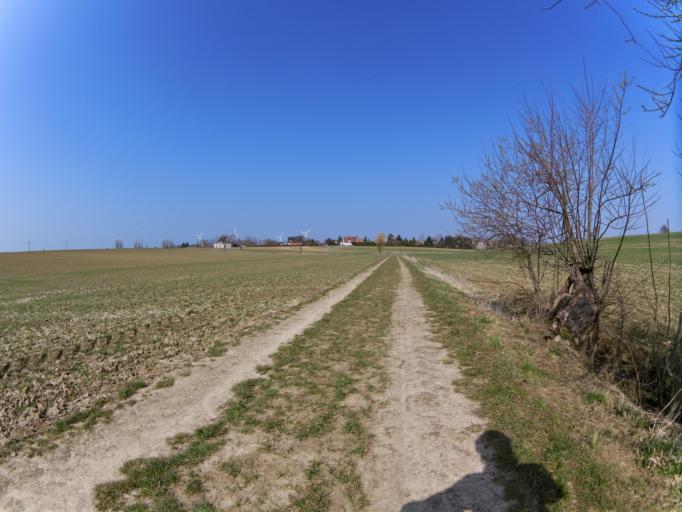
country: DE
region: Bavaria
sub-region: Regierungsbezirk Unterfranken
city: Geroldshausen
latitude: 49.6792
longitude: 9.9067
